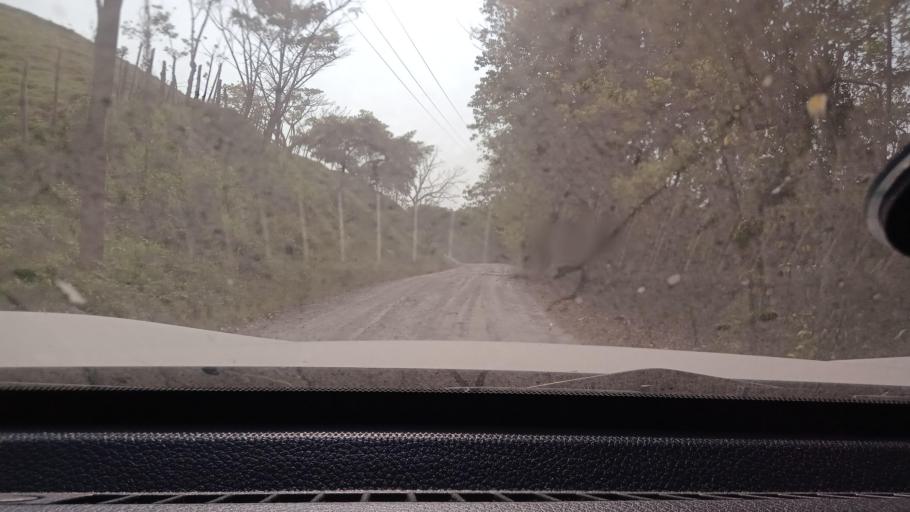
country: MX
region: Tabasco
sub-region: Huimanguillo
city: Francisco Rueda
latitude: 17.6204
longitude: -93.9467
